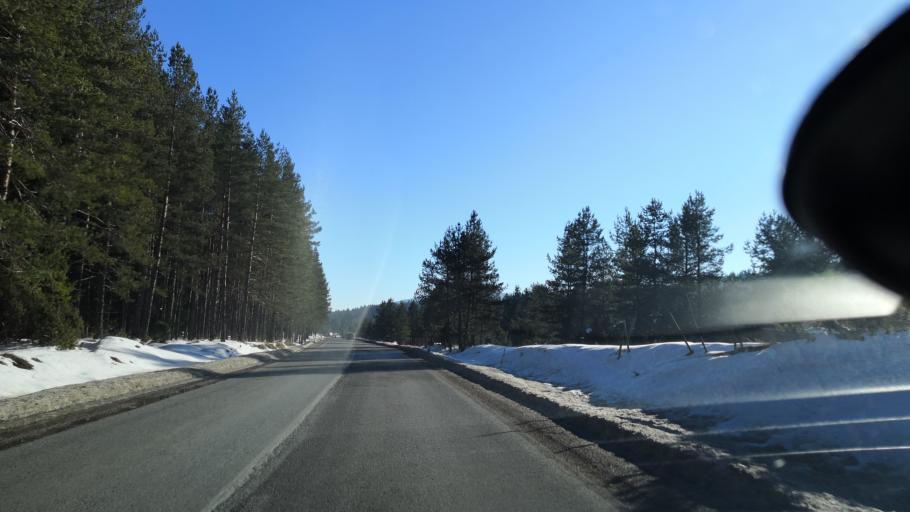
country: BA
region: Republika Srpska
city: Sokolac
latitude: 43.9148
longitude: 18.7012
